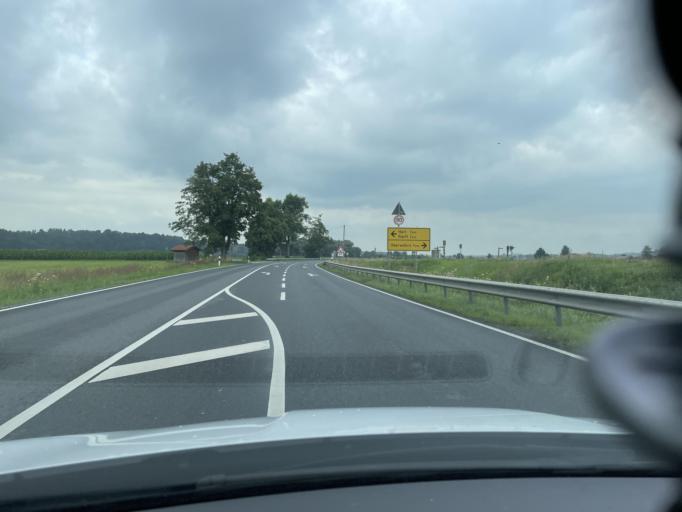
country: DE
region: Bavaria
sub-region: Upper Bavaria
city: Schechen
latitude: 47.9615
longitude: 12.1289
